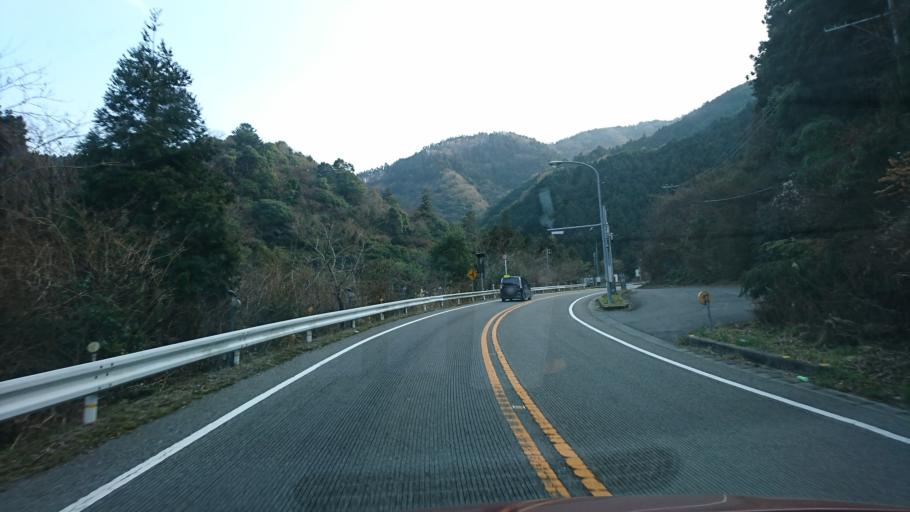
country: JP
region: Ehime
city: Hojo
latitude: 33.9557
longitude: 132.9117
